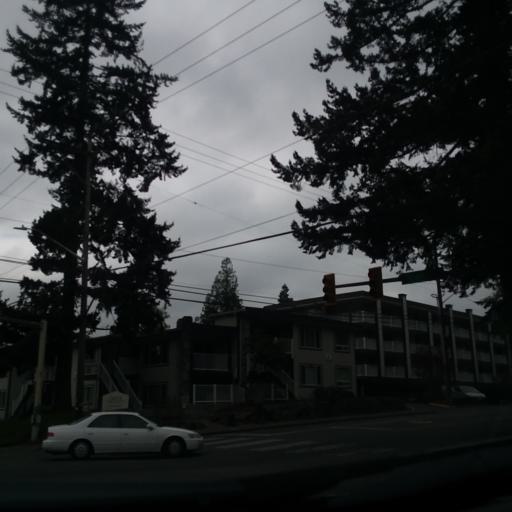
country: US
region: Washington
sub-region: King County
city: Boulevard Park
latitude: 47.4996
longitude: -122.3337
